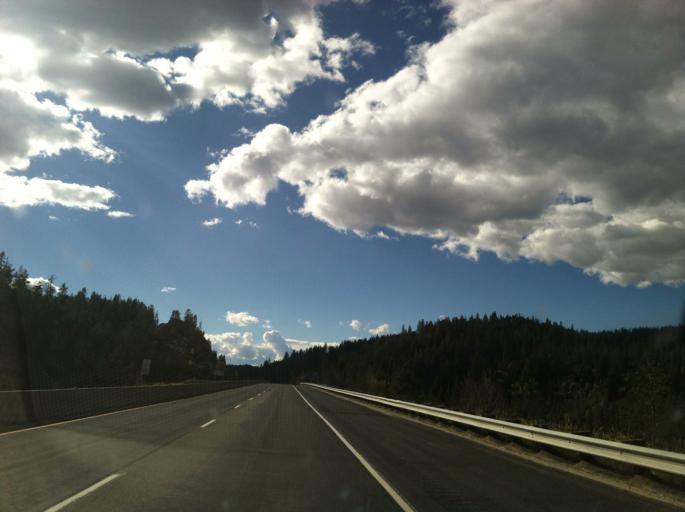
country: US
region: Montana
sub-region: Silver Bow County
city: Butte
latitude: 45.9144
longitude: -112.3639
